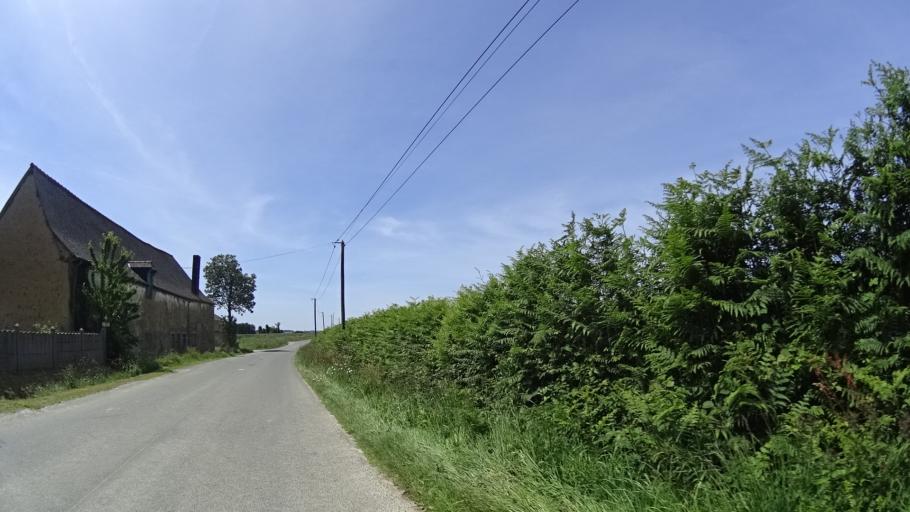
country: FR
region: Brittany
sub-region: Departement d'Ille-et-Vilaine
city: Romille
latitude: 48.1934
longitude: -1.8763
